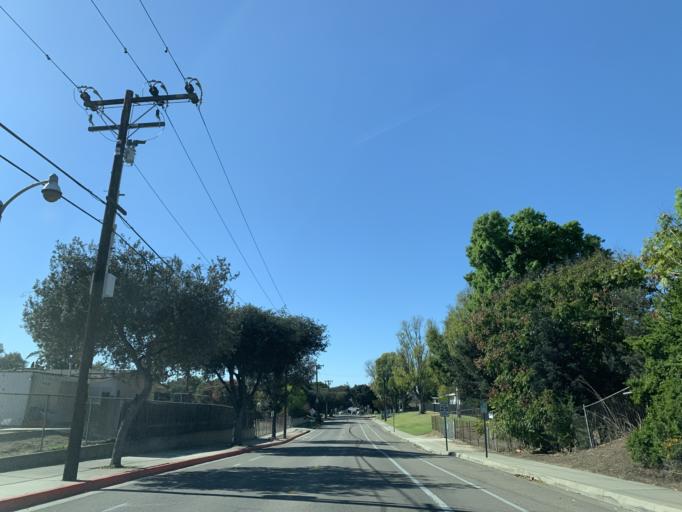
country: US
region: California
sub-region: Orange County
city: Placentia
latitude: 33.8814
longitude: -117.8960
